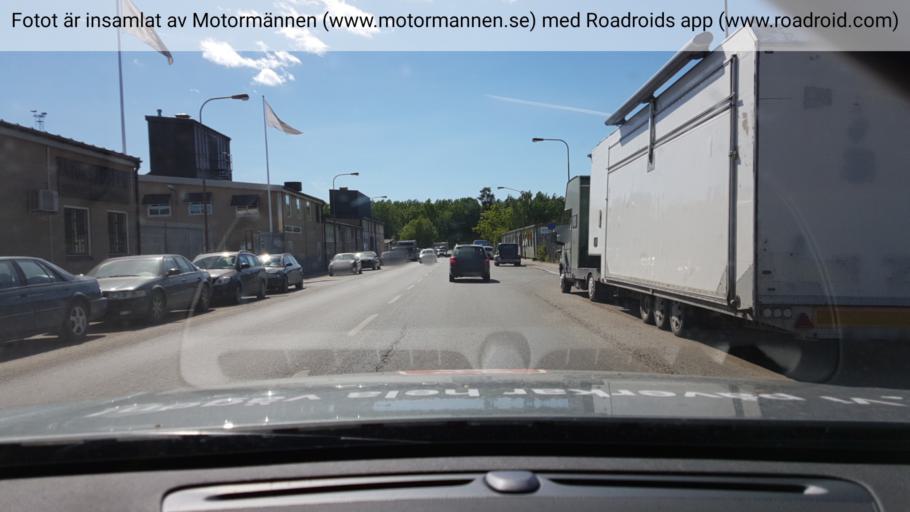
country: SE
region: Stockholm
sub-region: Stockholms Kommun
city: Arsta
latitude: 59.2594
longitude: 18.0515
